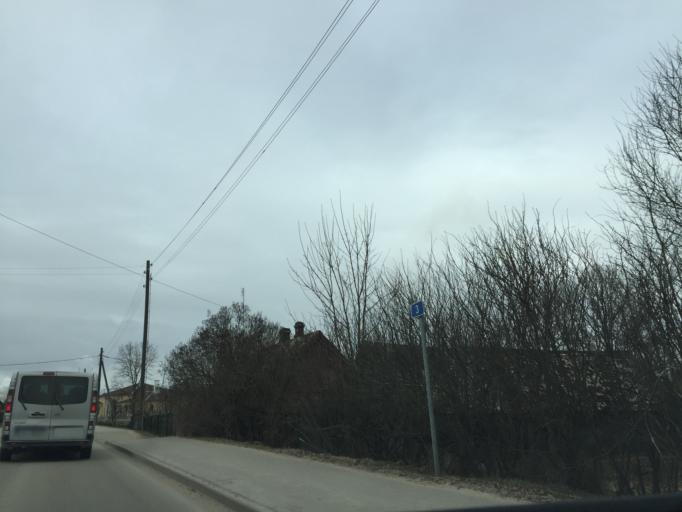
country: LV
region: Kraslavas Rajons
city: Kraslava
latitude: 55.9236
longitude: 27.1467
